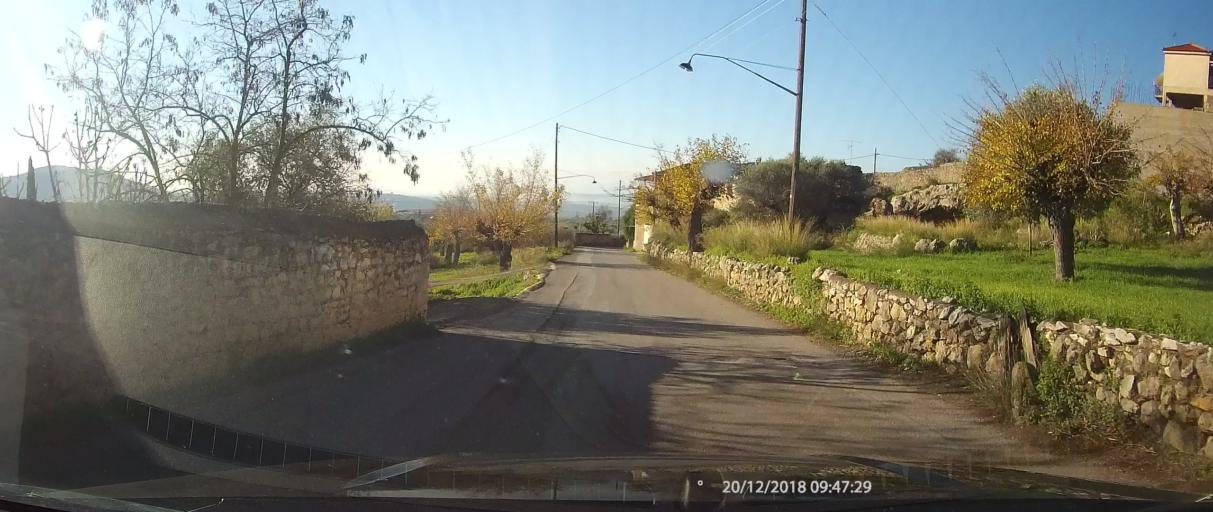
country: GR
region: Peloponnese
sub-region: Nomos Lakonias
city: Yerakion
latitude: 36.9909
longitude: 22.7084
